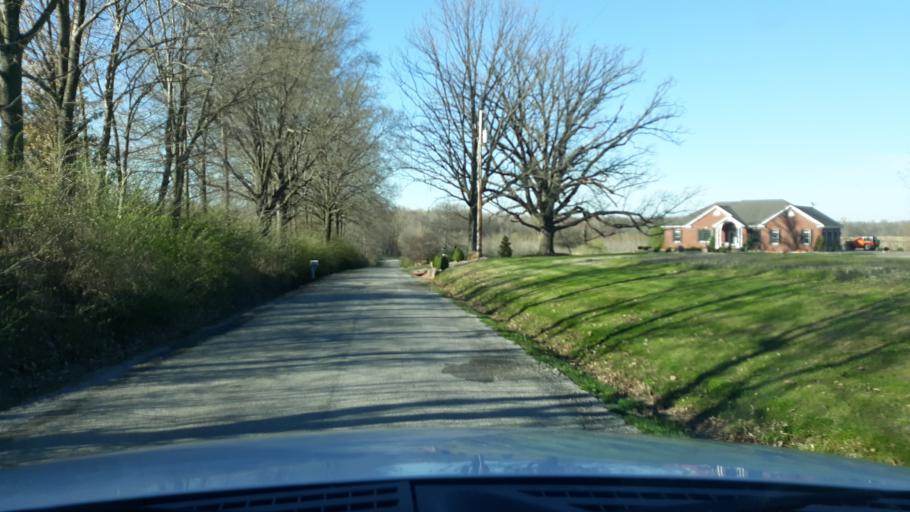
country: US
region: Illinois
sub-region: Saline County
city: Harrisburg
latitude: 37.7540
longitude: -88.5680
